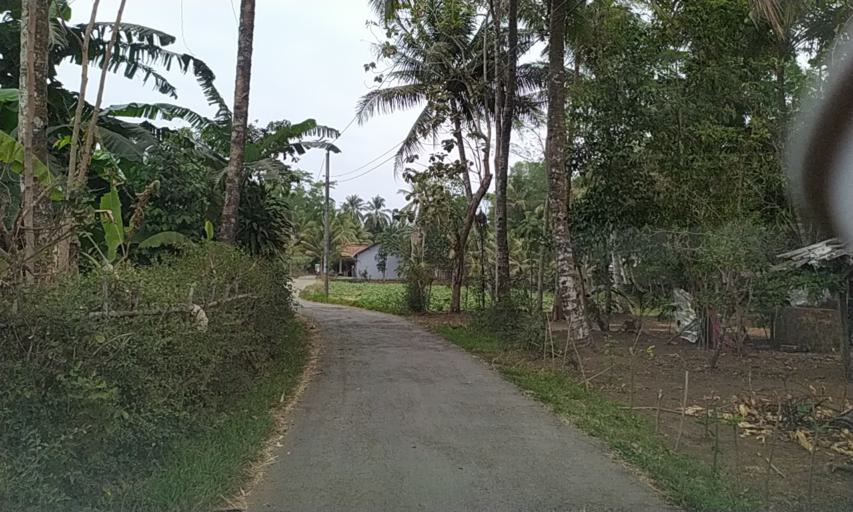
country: ID
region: Central Java
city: Kroya
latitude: -7.6951
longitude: 109.3127
